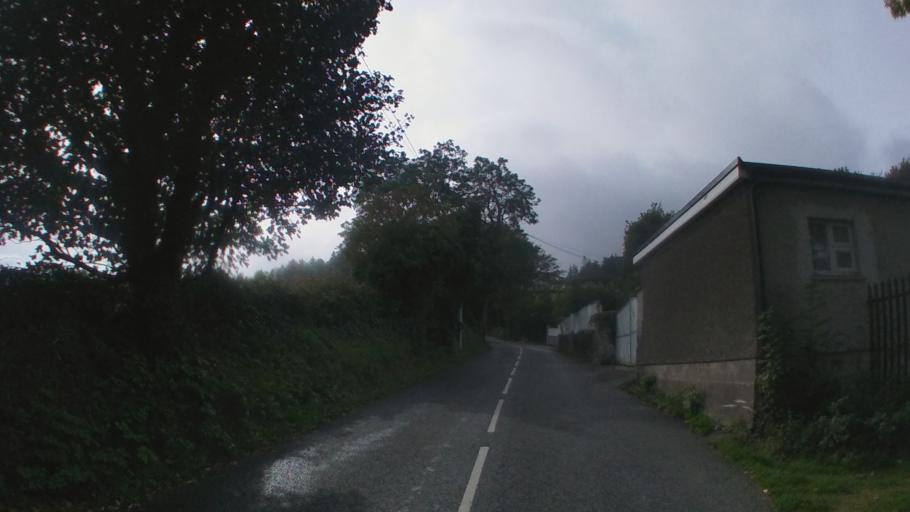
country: IE
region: Leinster
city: Sandyford
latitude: 53.2493
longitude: -6.2150
